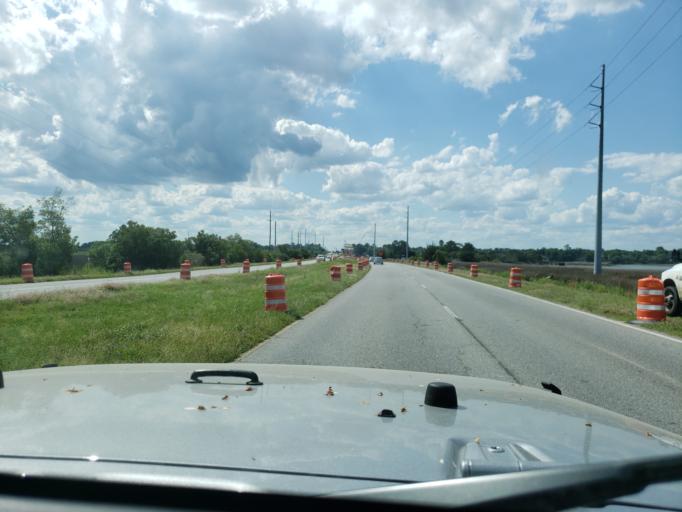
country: US
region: Georgia
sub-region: Chatham County
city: Whitemarsh Island
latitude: 32.0571
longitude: -81.0195
